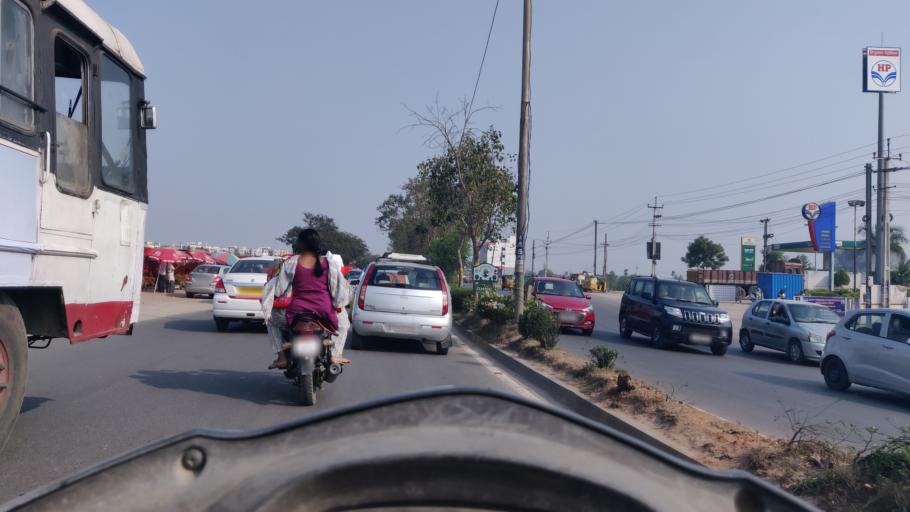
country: IN
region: Telangana
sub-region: Rangareddi
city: Uppal Kalan
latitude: 17.4022
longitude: 78.5762
